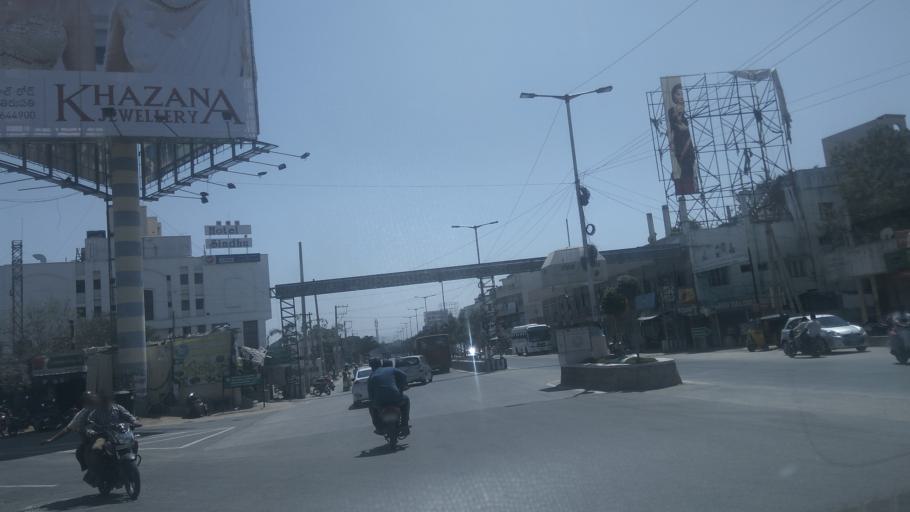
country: IN
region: Andhra Pradesh
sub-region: Chittoor
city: Tirupati
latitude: 13.6112
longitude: 79.4433
